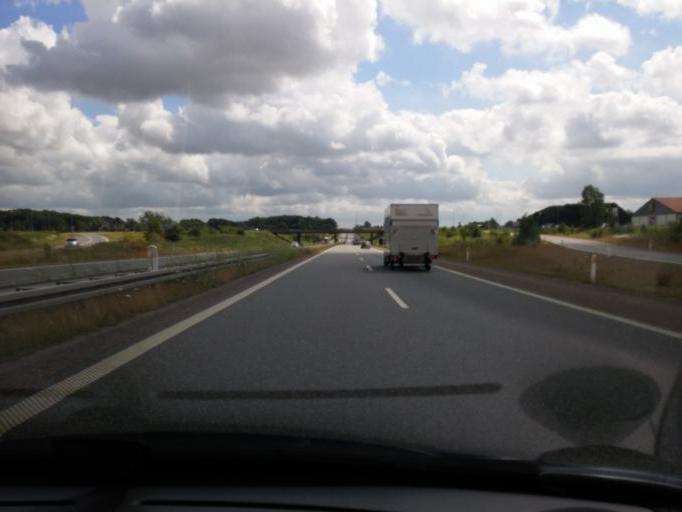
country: DK
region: South Denmark
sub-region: Faaborg-Midtfyn Kommune
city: Ringe
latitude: 55.2388
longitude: 10.4907
